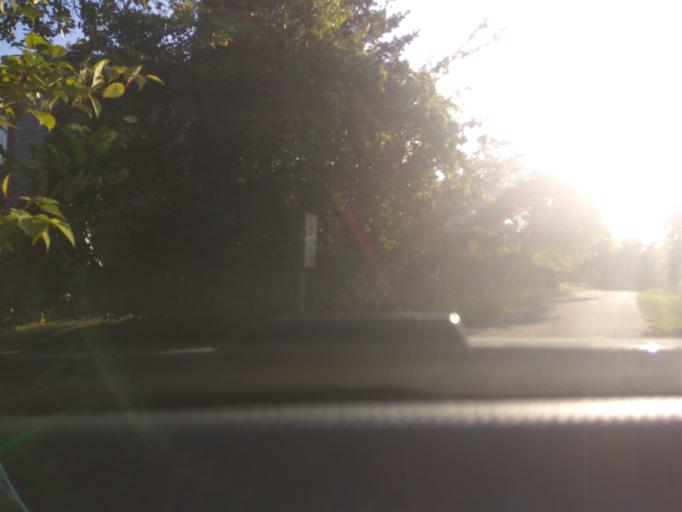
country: LV
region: Grobina
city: Grobina
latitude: 56.5312
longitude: 21.1756
